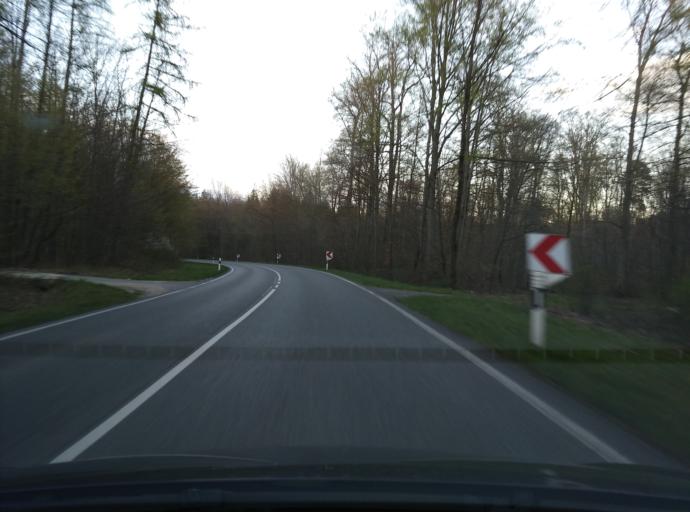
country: DE
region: Baden-Wuerttemberg
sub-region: Regierungsbezirk Stuttgart
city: Kohlberg
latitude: 48.5690
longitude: 9.3164
